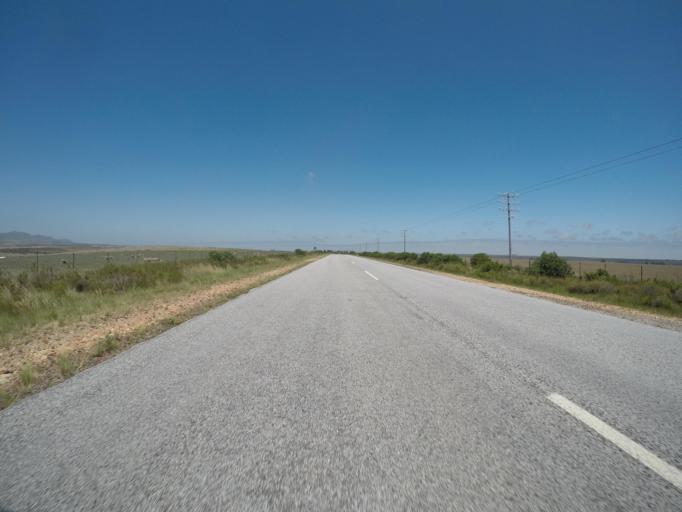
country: ZA
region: Eastern Cape
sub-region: Cacadu District Municipality
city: Kruisfontein
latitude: -34.0134
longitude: 24.5648
